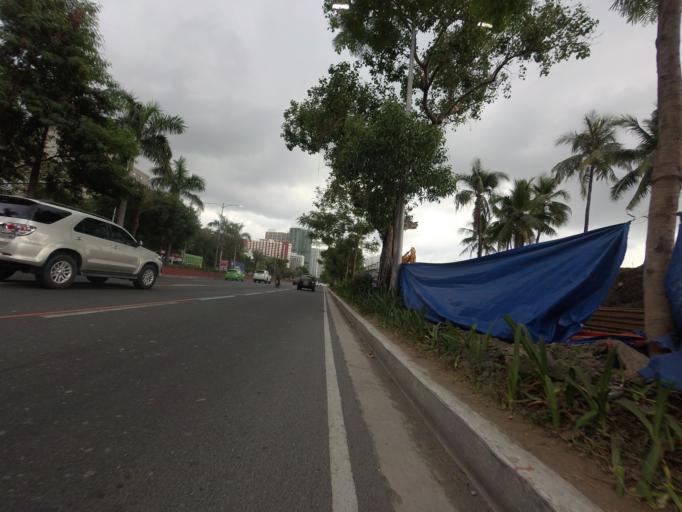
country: PH
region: Metro Manila
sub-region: City of Manila
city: Port Area
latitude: 14.5637
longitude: 120.9851
